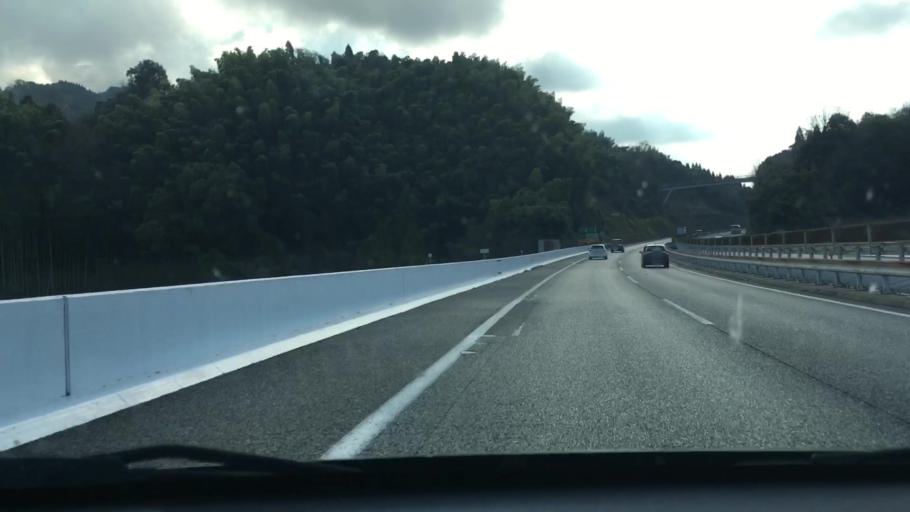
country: JP
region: Kumamoto
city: Yatsushiro
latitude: 32.5502
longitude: 130.6923
